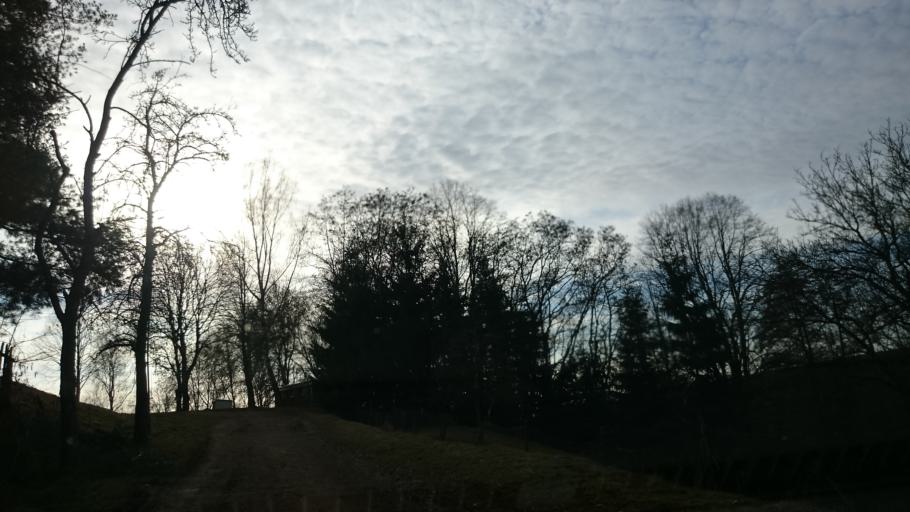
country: DE
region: Saxony
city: Sankt Egidien
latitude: 50.8043
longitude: 12.6409
